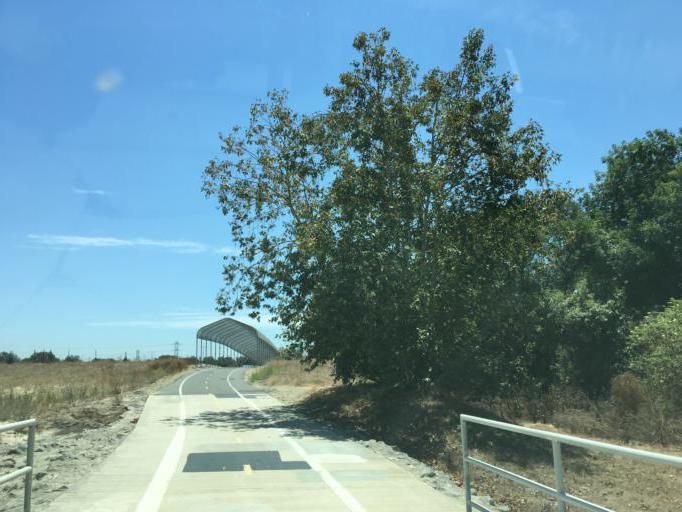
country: US
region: California
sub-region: Los Angeles County
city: South San Gabriel
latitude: 34.0465
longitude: -118.0714
